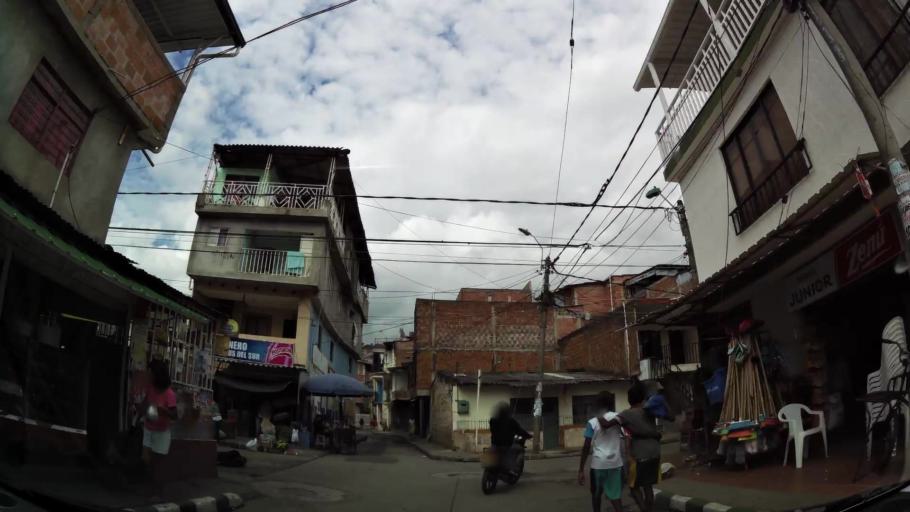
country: CO
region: Valle del Cauca
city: Cali
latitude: 3.3905
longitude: -76.5554
